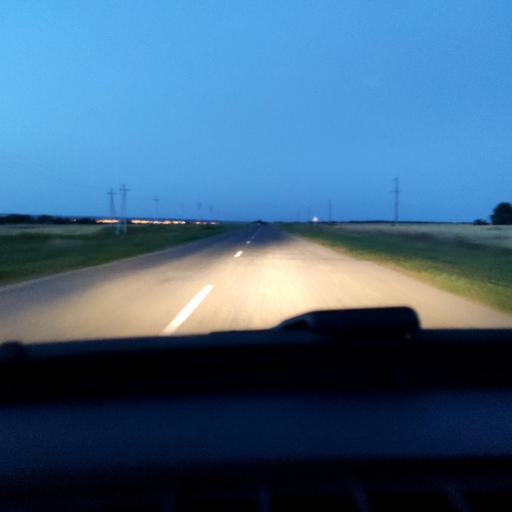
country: RU
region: Lipetsk
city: Zadonsk
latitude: 52.3107
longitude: 38.8990
